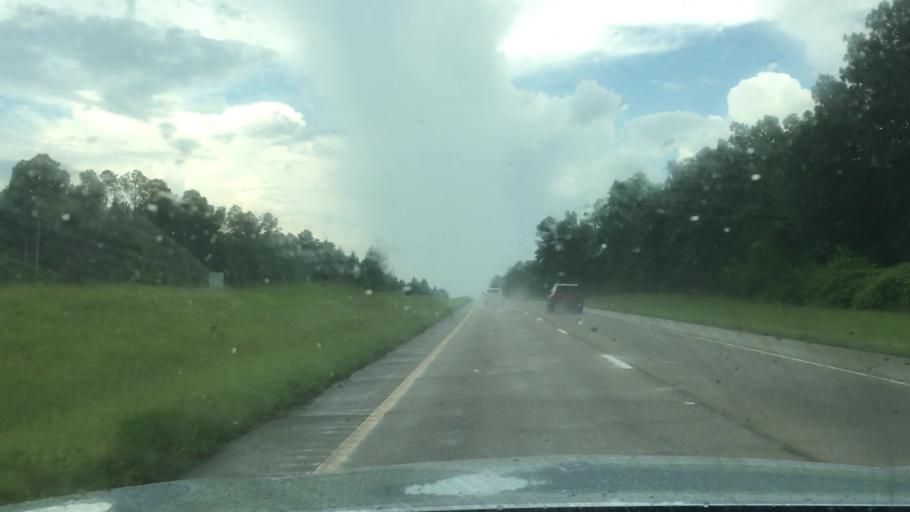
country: US
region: Mississippi
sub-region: Lamar County
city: Purvis
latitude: 31.1537
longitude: -89.3606
